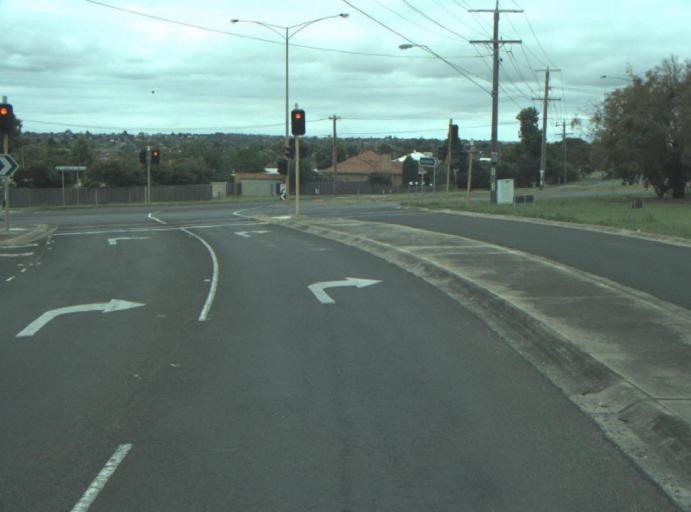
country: AU
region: Victoria
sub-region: Greater Geelong
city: Breakwater
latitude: -38.1812
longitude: 144.3363
